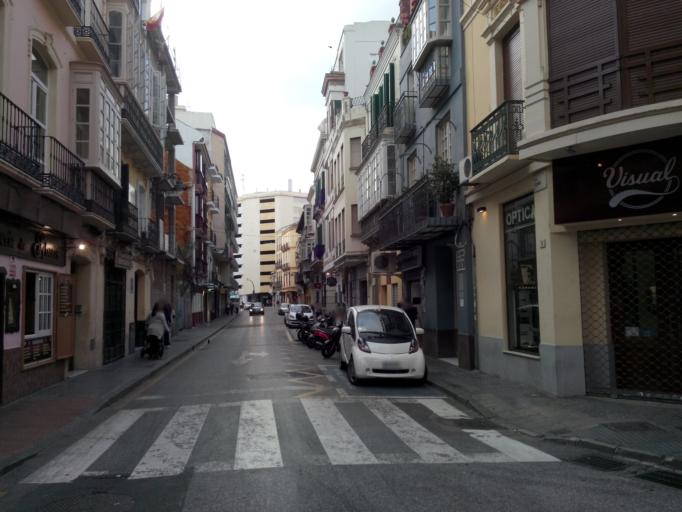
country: ES
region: Andalusia
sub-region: Provincia de Malaga
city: Malaga
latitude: 36.7236
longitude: -4.4194
